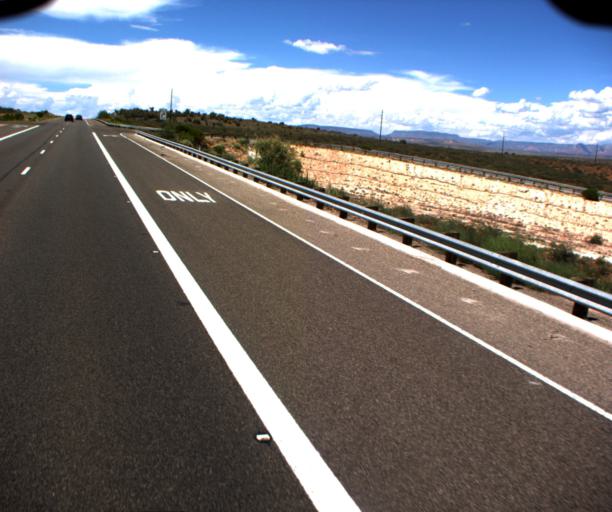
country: US
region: Arizona
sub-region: Yavapai County
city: Verde Village
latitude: 34.6798
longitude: -111.9734
